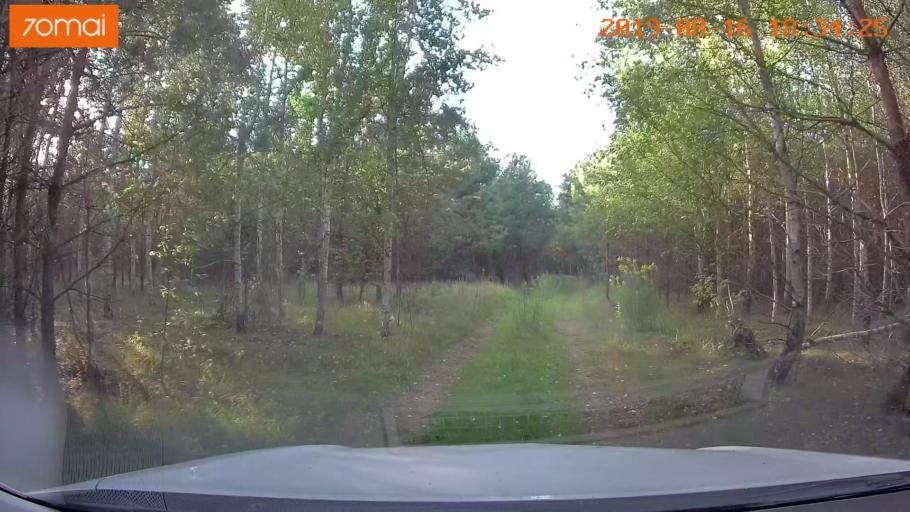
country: BY
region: Mogilev
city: Asipovichy
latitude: 53.2031
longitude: 28.6385
